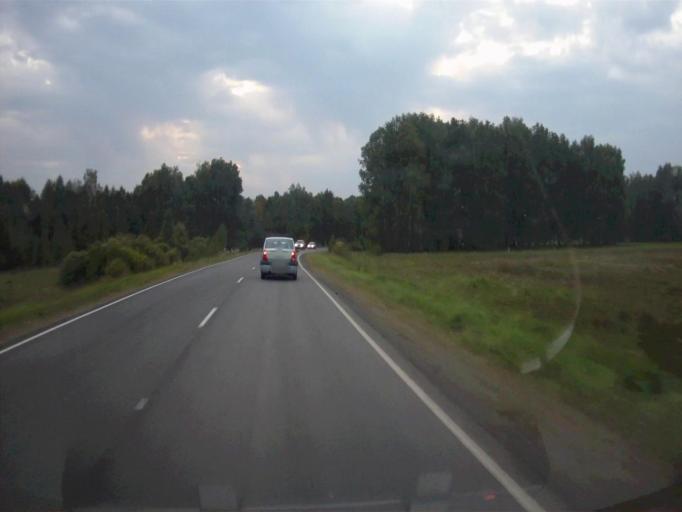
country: RU
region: Chelyabinsk
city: Chebarkul'
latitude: 55.1832
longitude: 60.4707
